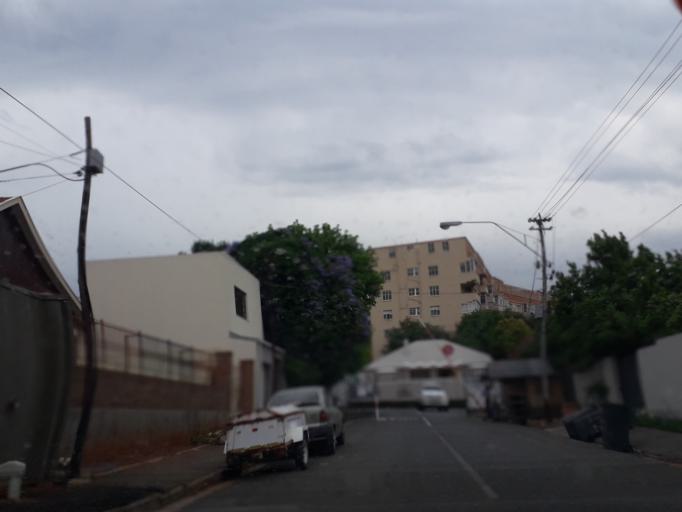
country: ZA
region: Gauteng
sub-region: City of Johannesburg Metropolitan Municipality
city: Johannesburg
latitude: -26.1667
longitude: 28.0765
